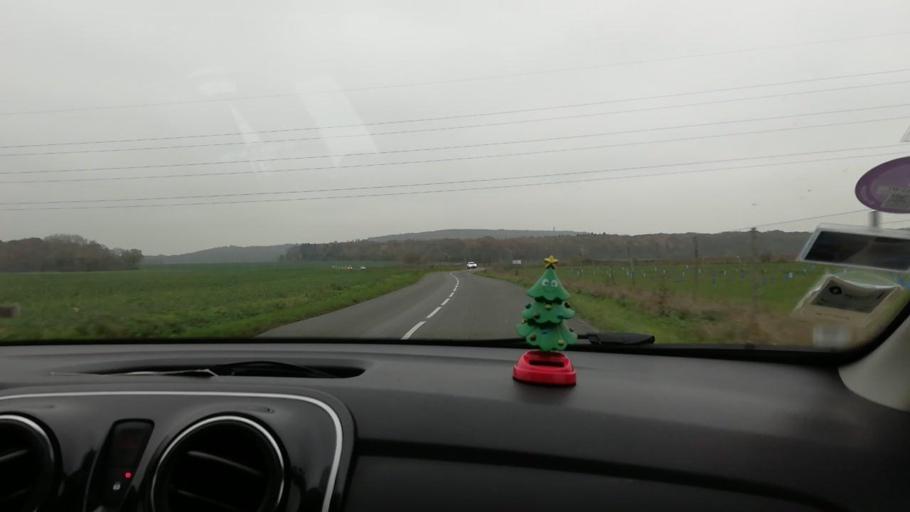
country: FR
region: Ile-de-France
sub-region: Departement de Seine-et-Marne
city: Saint-Mard
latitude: 49.0409
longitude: 2.7125
